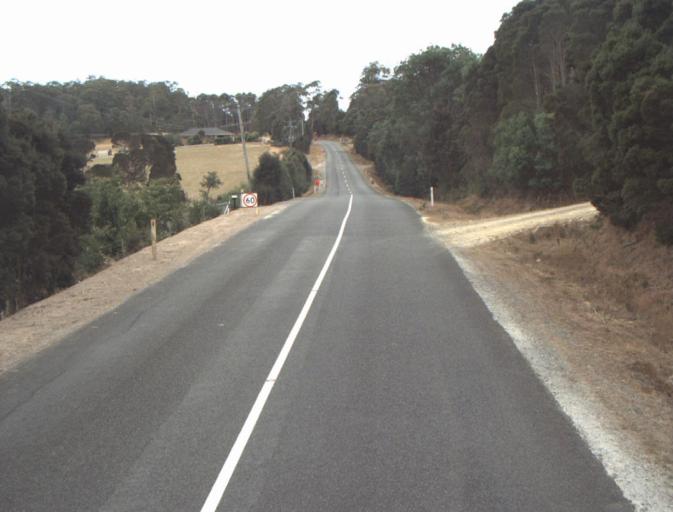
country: AU
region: Tasmania
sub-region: Launceston
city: Mayfield
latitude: -41.2354
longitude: 147.0202
